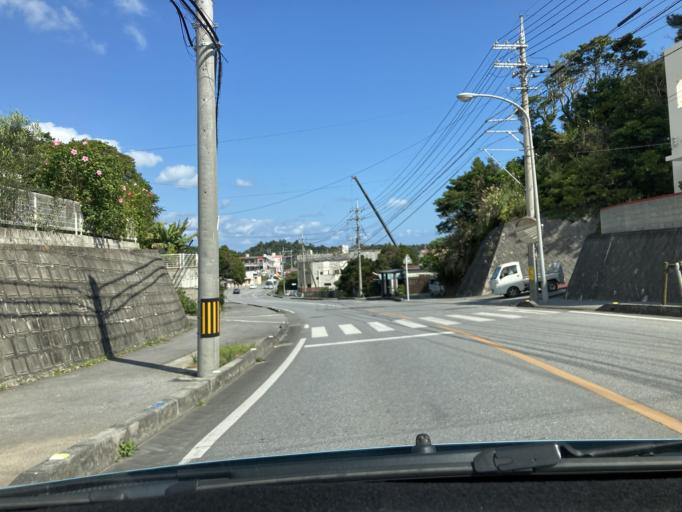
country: JP
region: Okinawa
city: Nago
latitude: 26.6198
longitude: 127.9993
